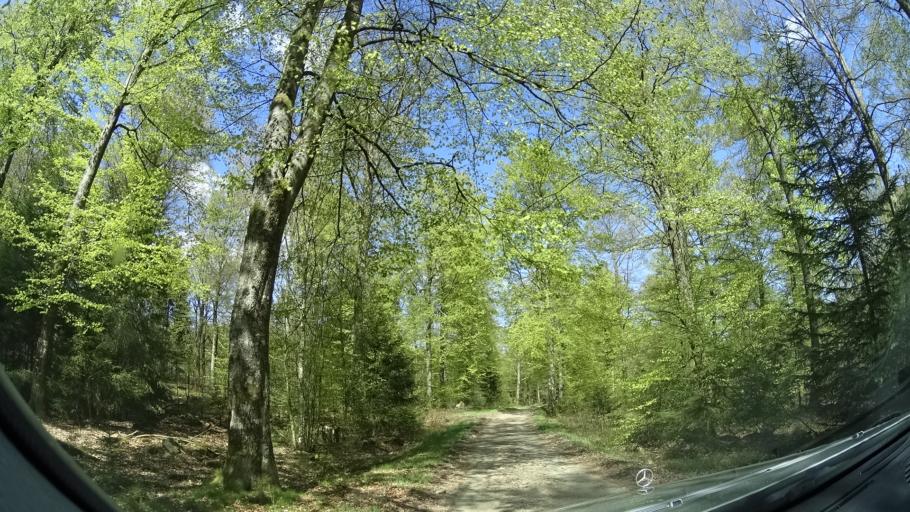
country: SE
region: Skane
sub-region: Hassleholms Kommun
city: Tormestorp
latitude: 56.0937
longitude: 13.6926
